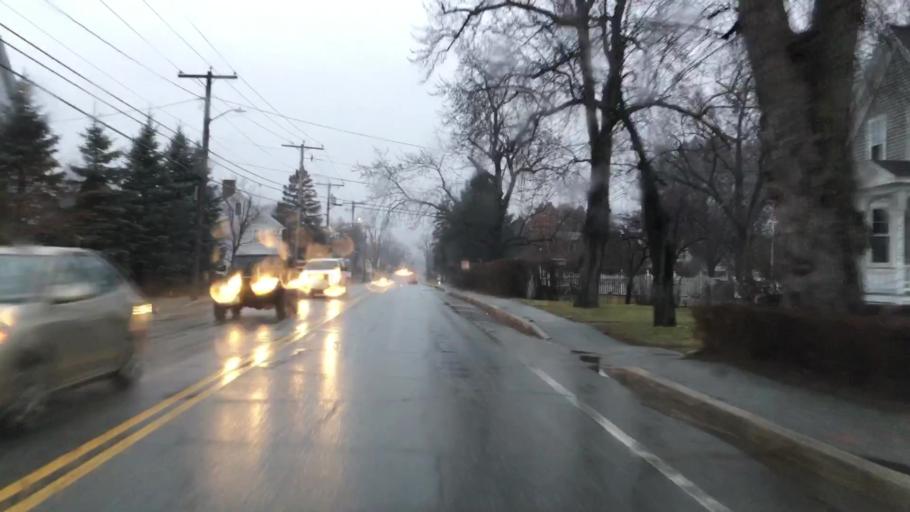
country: US
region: New Hampshire
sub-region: Hillsborough County
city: Milford
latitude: 42.8302
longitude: -71.6370
